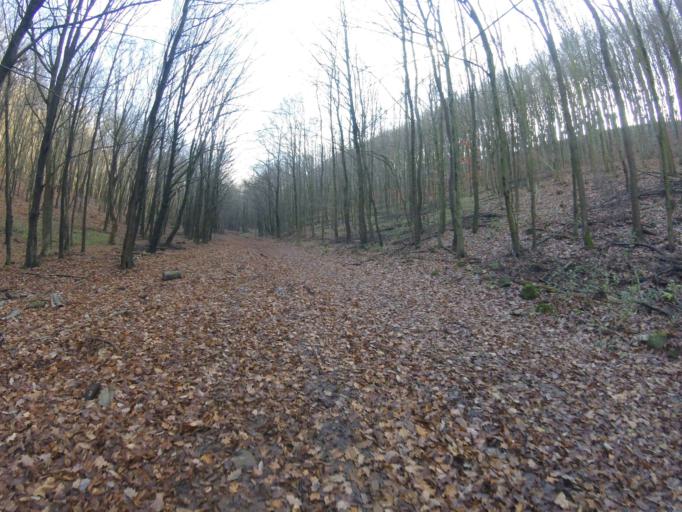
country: HU
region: Pest
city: Szob
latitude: 47.9060
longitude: 18.8784
